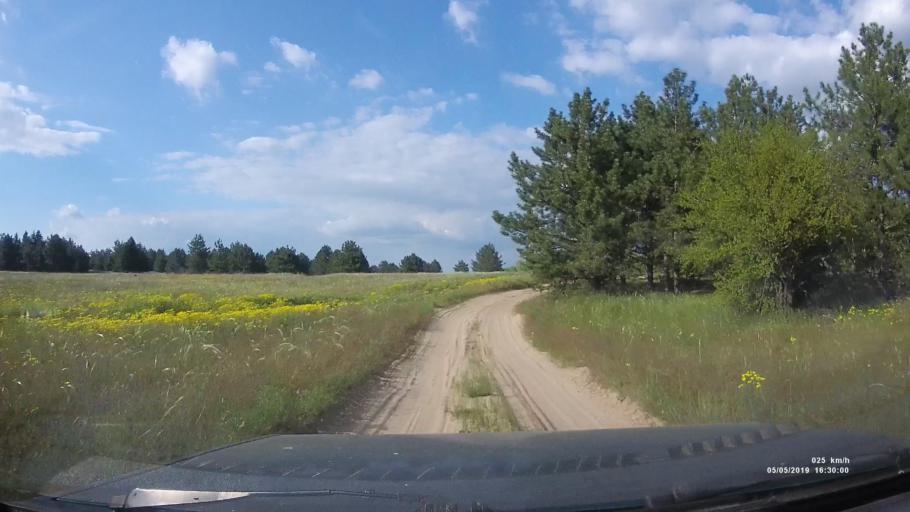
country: RU
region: Rostov
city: Ust'-Donetskiy
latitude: 47.7723
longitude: 41.0151
